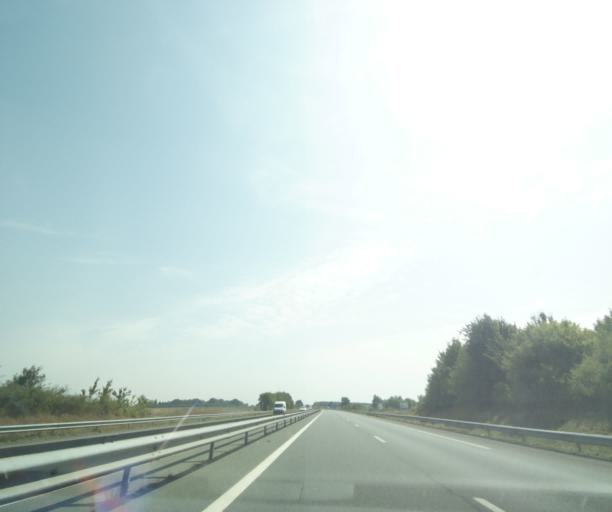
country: FR
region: Pays de la Loire
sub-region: Departement de la Vendee
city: Sainte-Hermine
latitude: 46.5290
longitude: -1.0671
